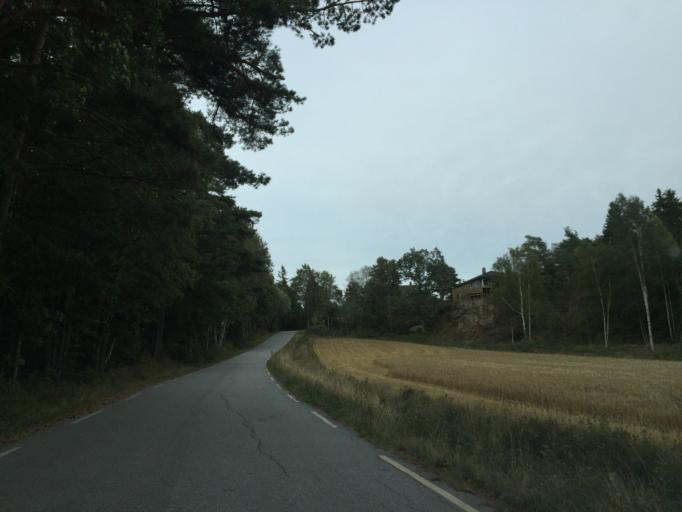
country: NO
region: Ostfold
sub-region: Hvaler
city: Skjaerhalden
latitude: 59.0558
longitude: 11.0566
